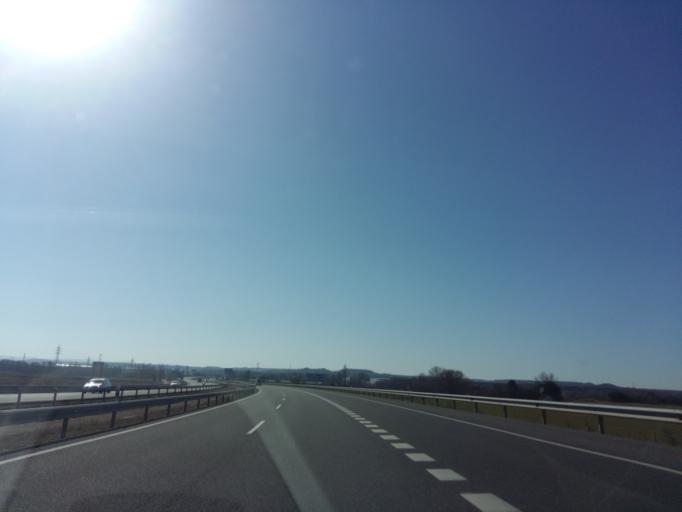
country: ES
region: Castille and Leon
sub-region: Provincia de Burgos
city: Villalba de Duero
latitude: 41.6745
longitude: -3.7294
